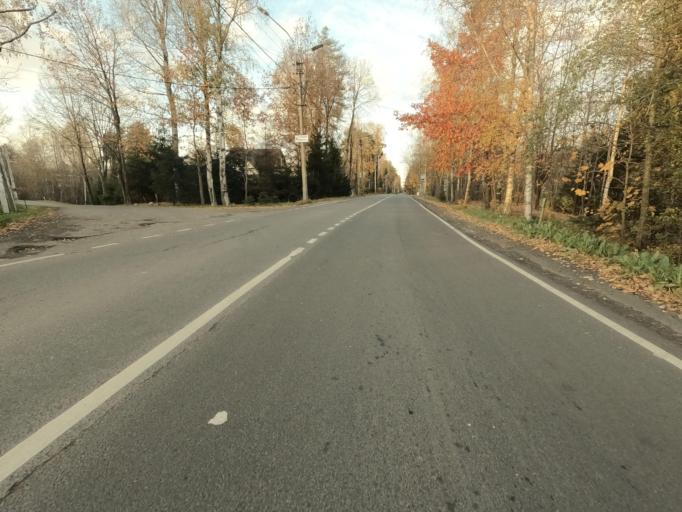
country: RU
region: St.-Petersburg
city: Beloostrov
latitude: 60.1603
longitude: 30.0058
